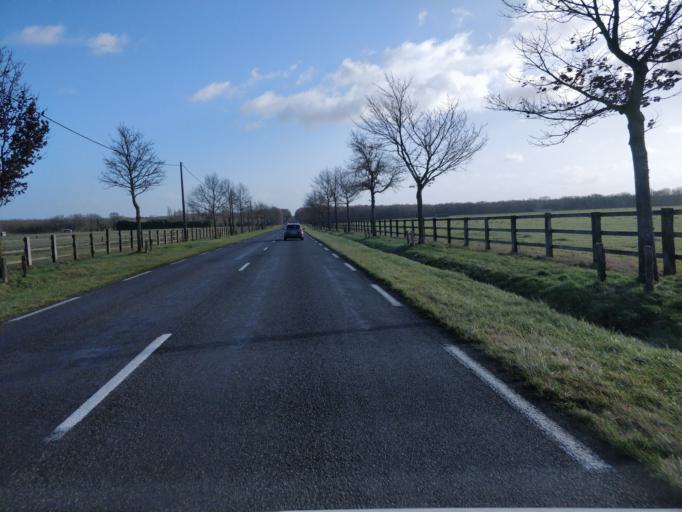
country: FR
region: Ile-de-France
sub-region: Departement de Seine-et-Marne
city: Bagneaux-sur-Loing
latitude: 48.2512
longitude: 2.7636
